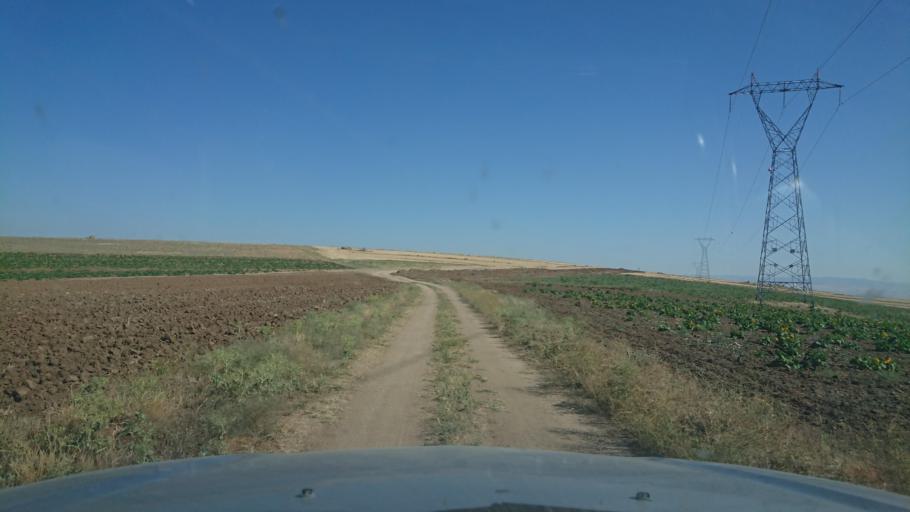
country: TR
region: Aksaray
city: Agacoren
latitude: 38.8364
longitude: 33.9452
